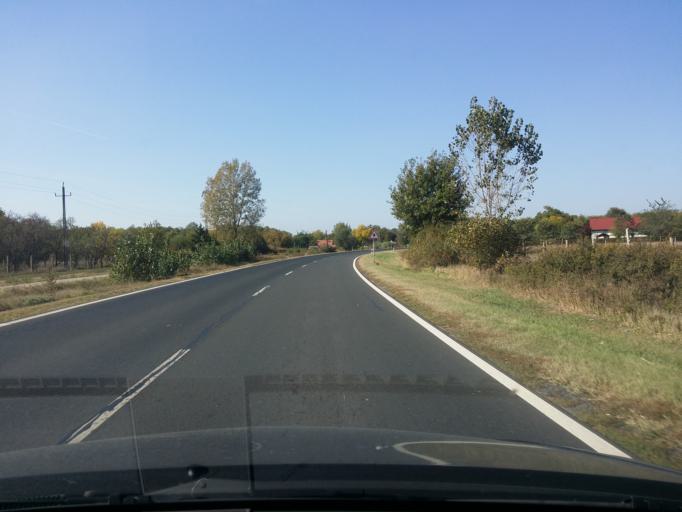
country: HU
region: Bacs-Kiskun
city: Nyarlorinc
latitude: 46.8688
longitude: 19.8592
